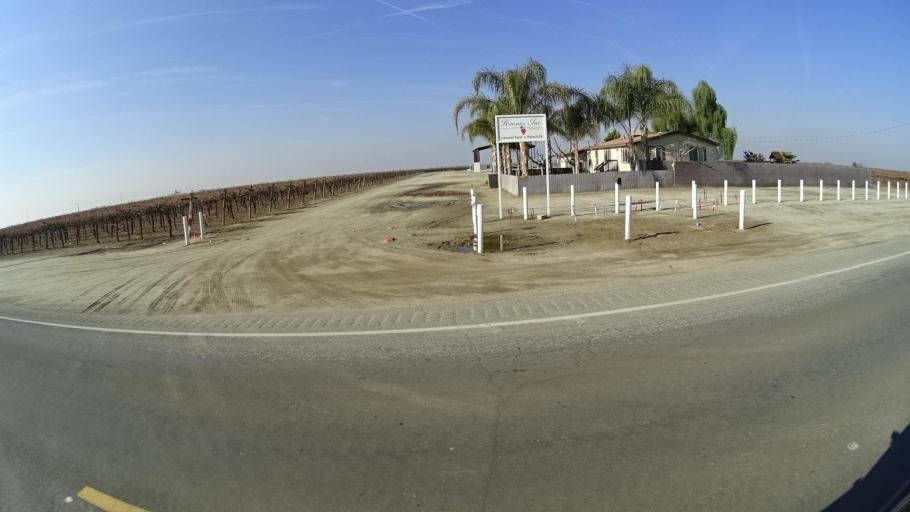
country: US
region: California
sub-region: Kern County
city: Weedpatch
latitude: 35.2277
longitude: -118.9322
